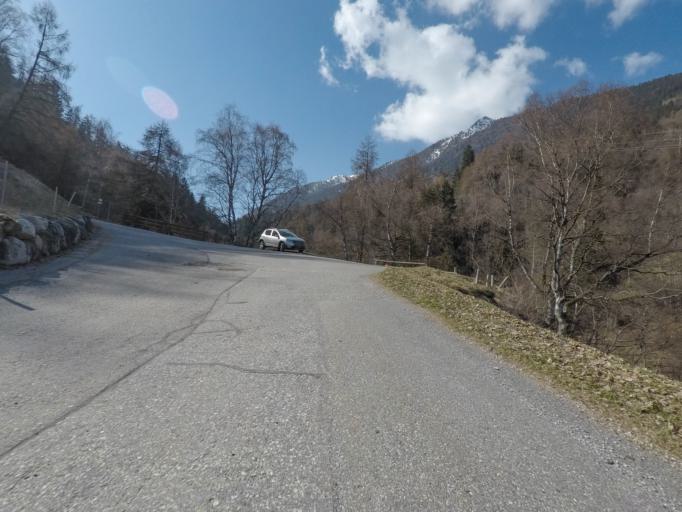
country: CH
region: Valais
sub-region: Conthey District
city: Basse-Nendaz
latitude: 46.1681
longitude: 7.3197
